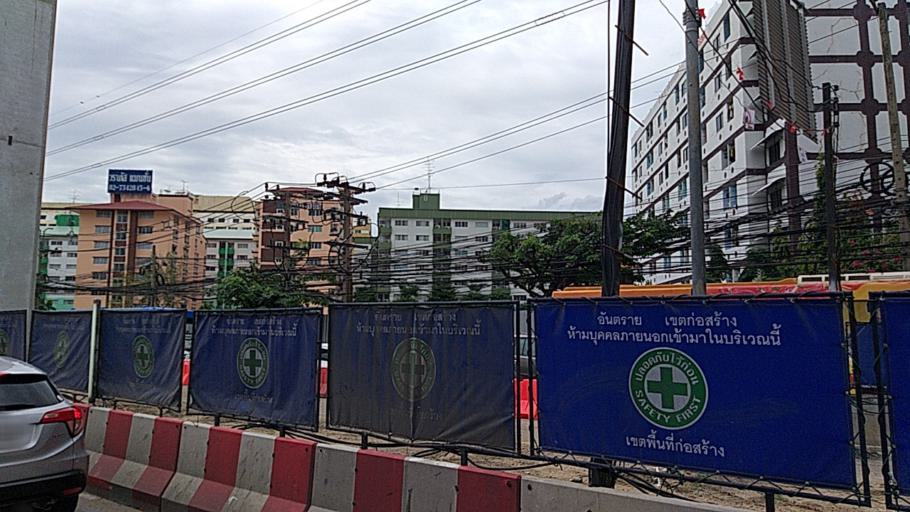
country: TH
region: Bangkok
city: Bang Kapi
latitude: 13.7700
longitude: 100.6379
